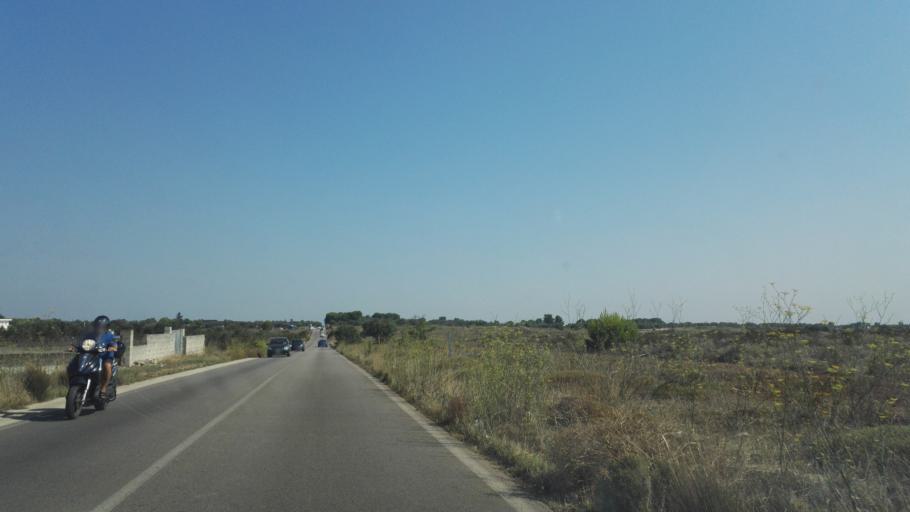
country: IT
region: Apulia
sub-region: Provincia di Lecce
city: Nardo
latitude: 40.1328
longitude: 18.0192
